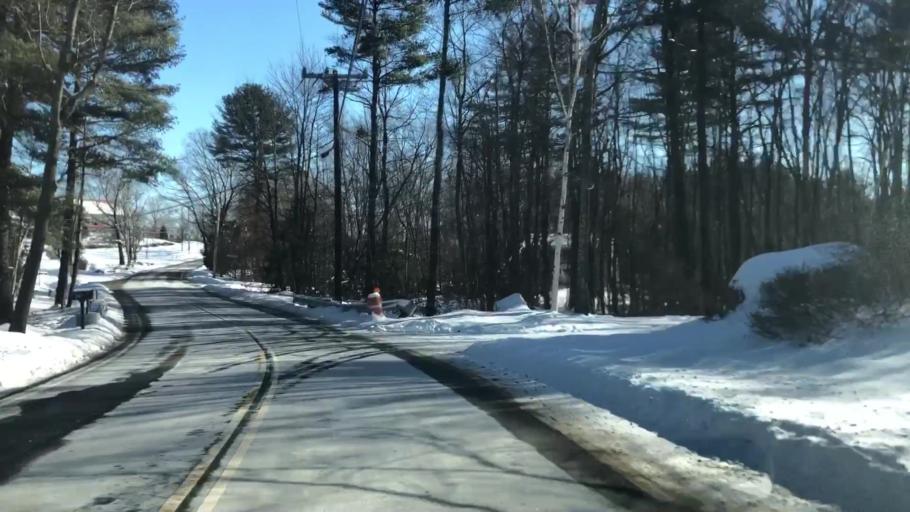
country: US
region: New Hampshire
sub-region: Hillsborough County
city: Bedford
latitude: 42.9424
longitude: -71.5439
